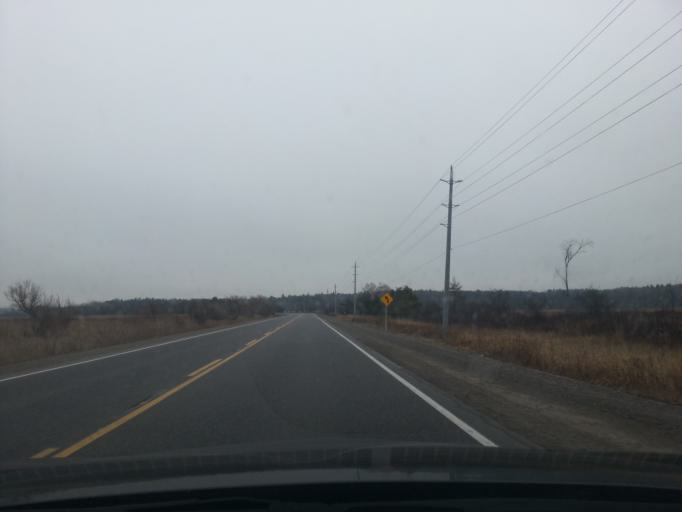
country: CA
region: Ontario
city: Oshawa
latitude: 44.1058
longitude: -78.8925
